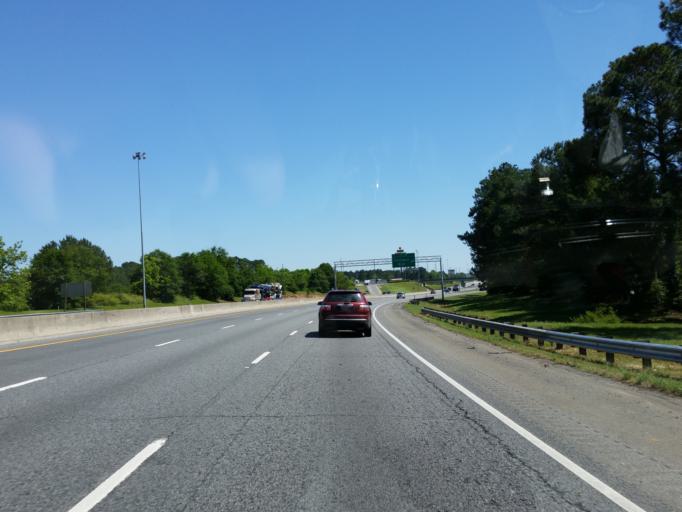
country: US
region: Georgia
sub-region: Tift County
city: Unionville
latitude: 31.4215
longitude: -83.5074
